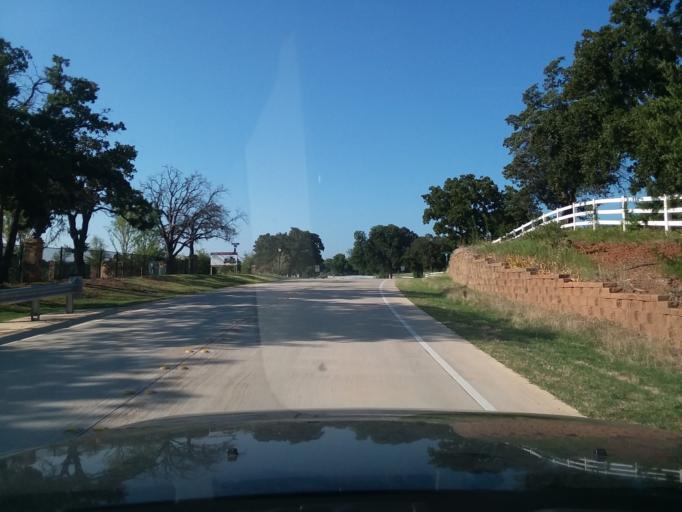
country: US
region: Texas
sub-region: Denton County
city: Copper Canyon
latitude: 33.0896
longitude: -97.0855
